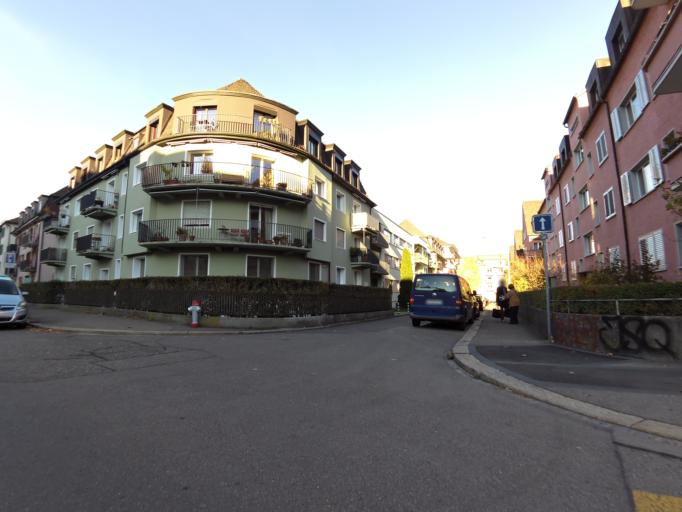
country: CH
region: Zurich
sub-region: Bezirk Zuerich
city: Zuerich (Kreis 3) / Sihlfeld
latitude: 47.3689
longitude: 8.5111
